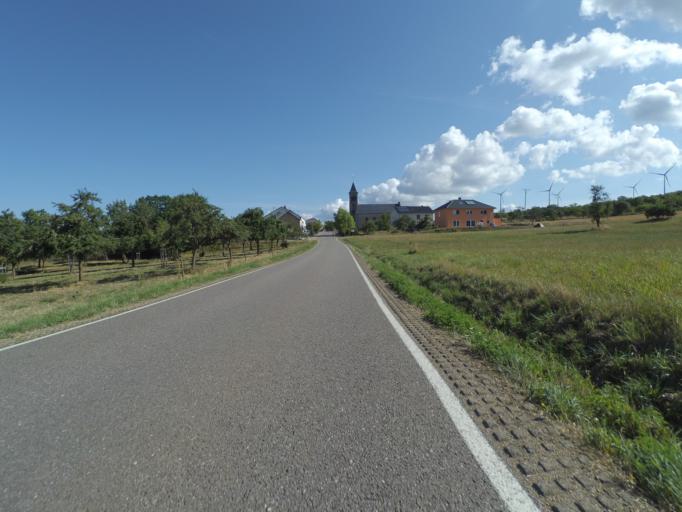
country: DE
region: Saarland
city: Perl
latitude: 49.5128
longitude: 6.4135
